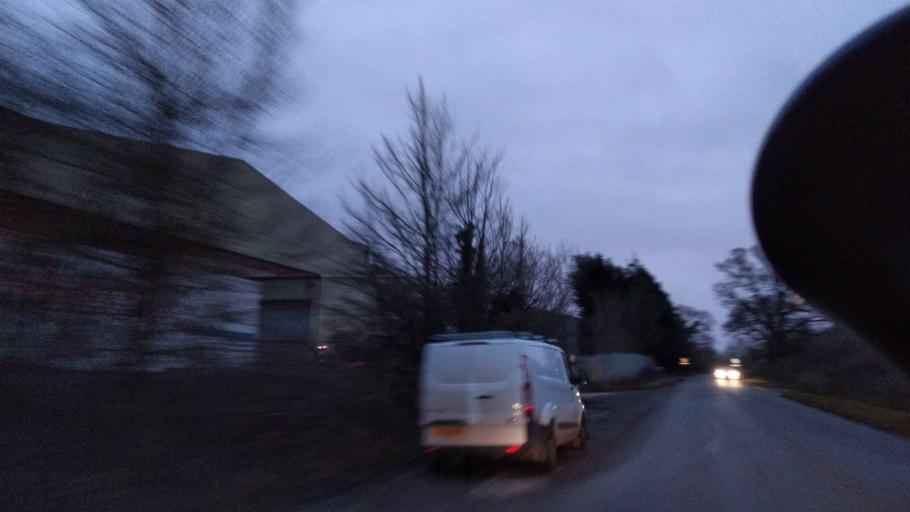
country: GB
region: England
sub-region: Borough of Swindon
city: Highworth
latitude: 51.5855
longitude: -1.7295
